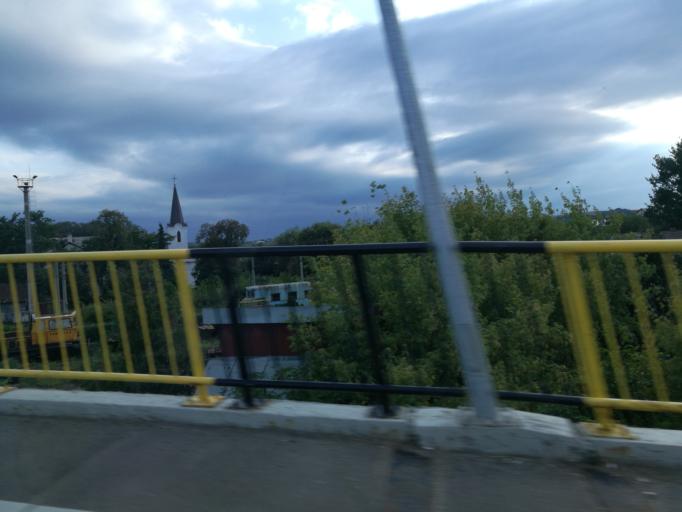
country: RO
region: Suceava
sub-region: Comuna Scheia
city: Scheia
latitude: 47.6762
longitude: 26.2400
